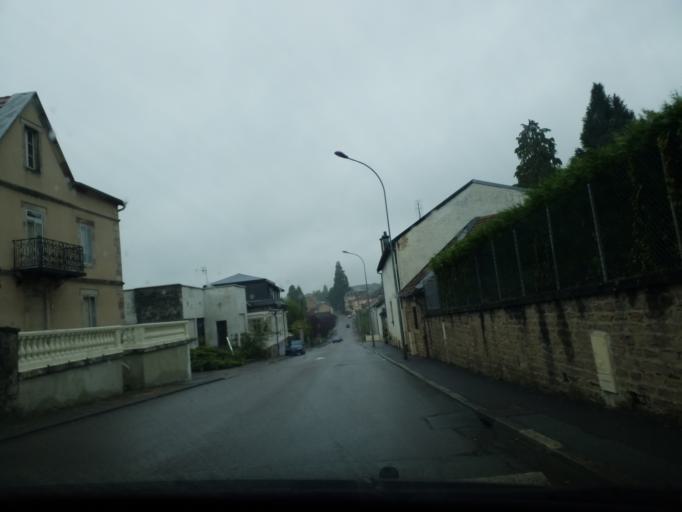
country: FR
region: Franche-Comte
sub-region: Departement de la Haute-Saone
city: Saint-Sauveur
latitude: 47.8130
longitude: 6.3779
